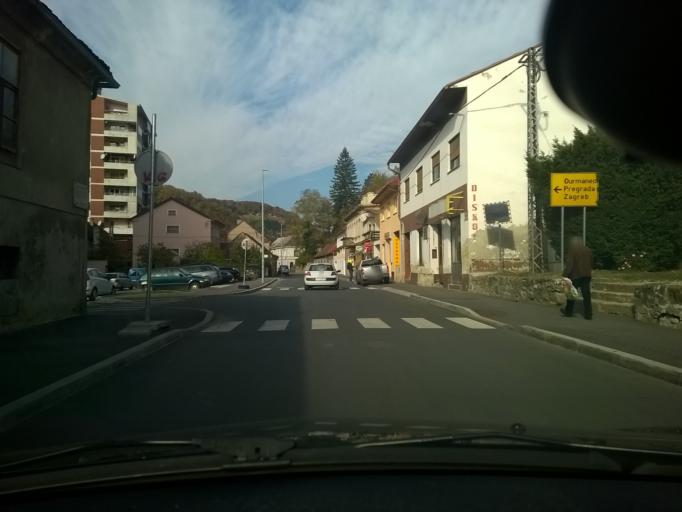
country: HR
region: Krapinsko-Zagorska
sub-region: Grad Krapina
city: Krapina
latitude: 46.1665
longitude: 15.8675
